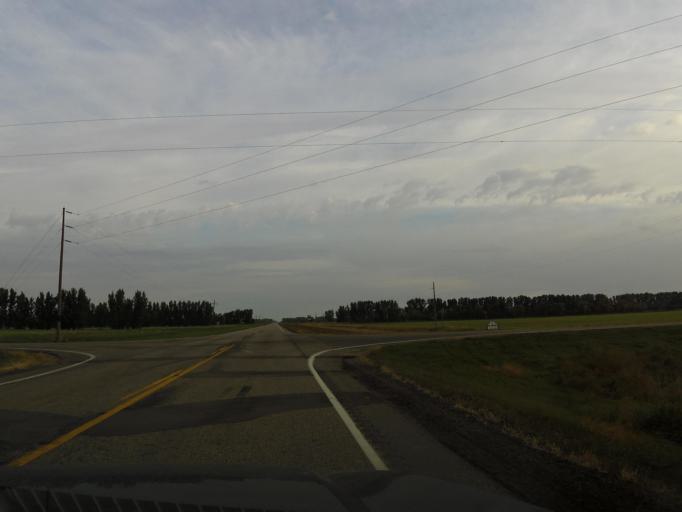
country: US
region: North Dakota
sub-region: Pembina County
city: Cavalier
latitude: 48.6878
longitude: -97.6230
